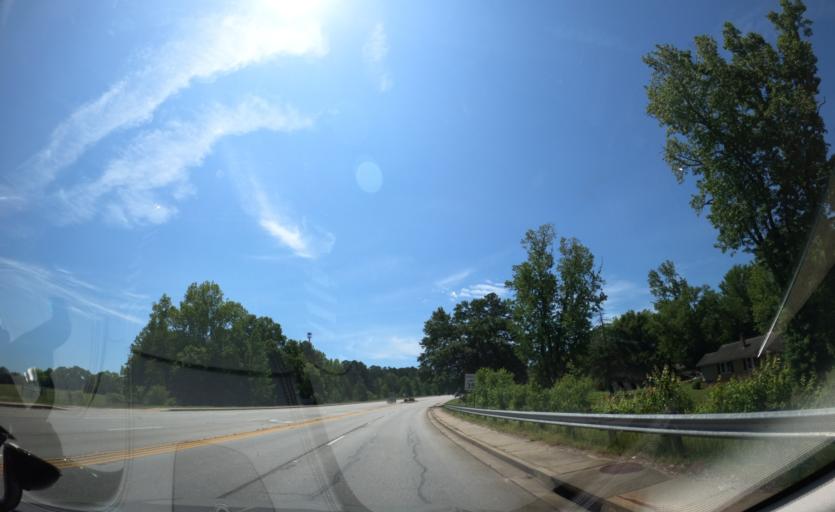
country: US
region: South Carolina
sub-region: Anderson County
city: Iva
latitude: 34.3196
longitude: -82.6644
